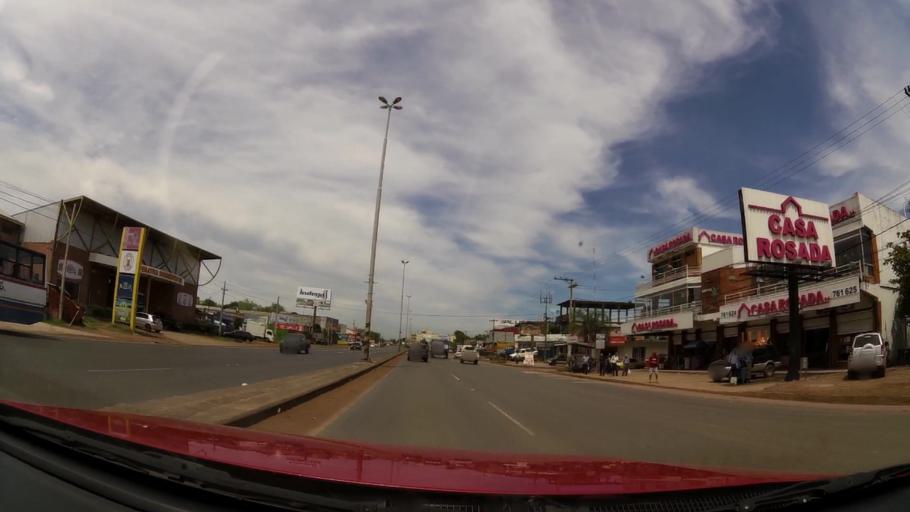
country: PY
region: Central
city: Colonia Mariano Roque Alonso
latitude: -25.2069
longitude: -57.5271
